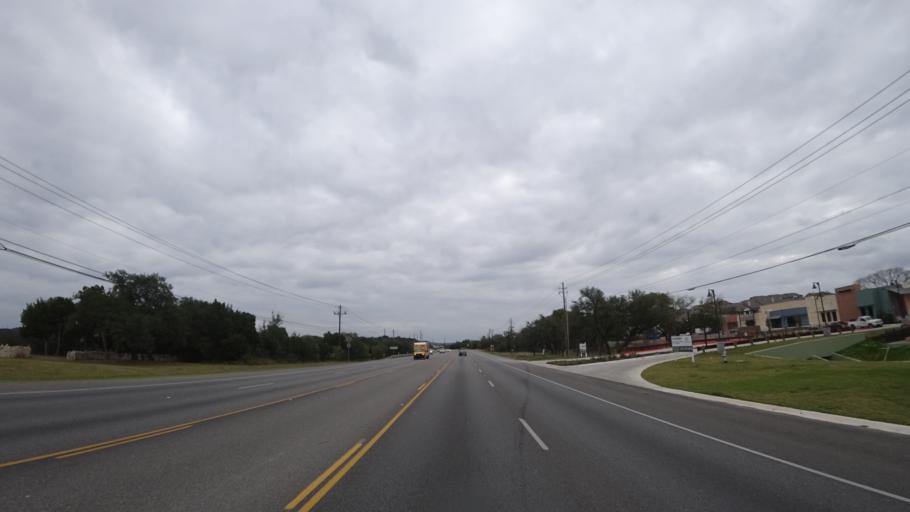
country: US
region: Texas
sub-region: Travis County
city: Bee Cave
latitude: 30.3239
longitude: -97.9571
